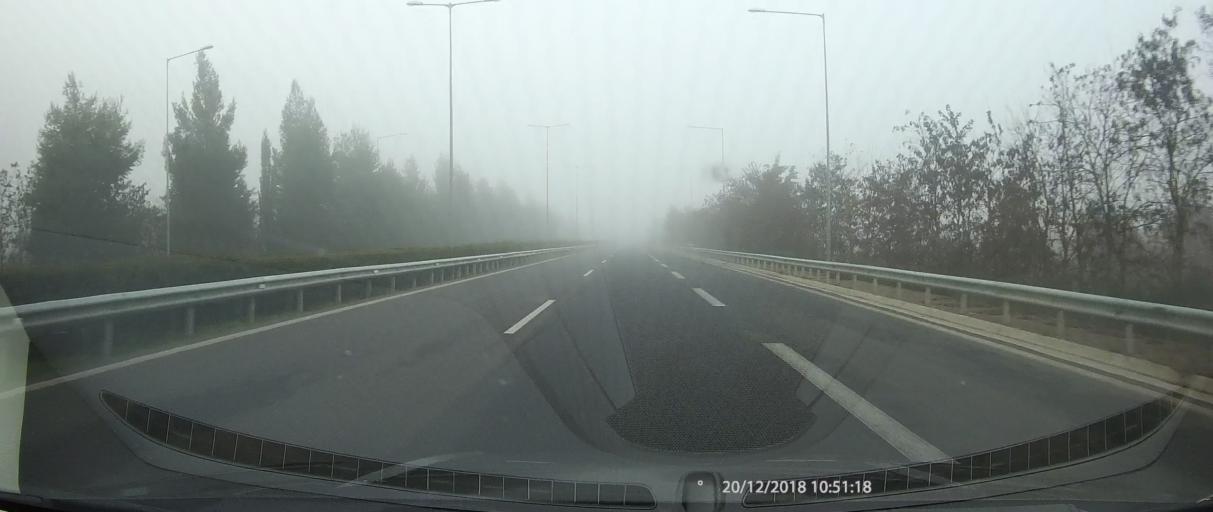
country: GR
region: Peloponnese
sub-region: Nomos Arkadias
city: Tripoli
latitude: 37.5833
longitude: 22.4330
